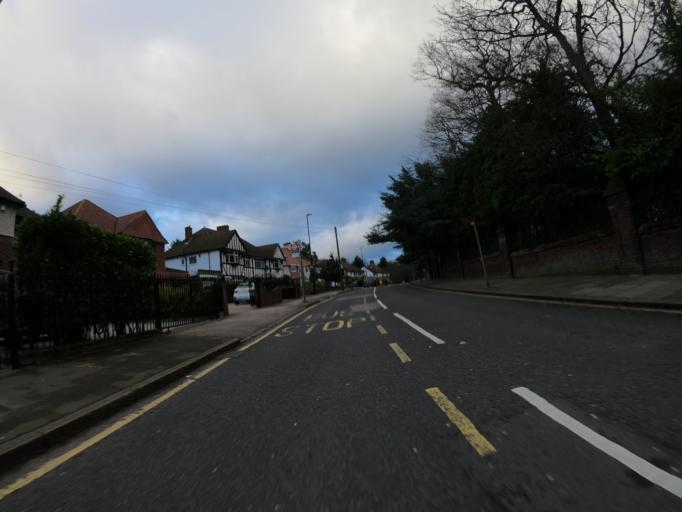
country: GB
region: England
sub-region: Greater London
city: Welling
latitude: 51.4571
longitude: 0.0767
